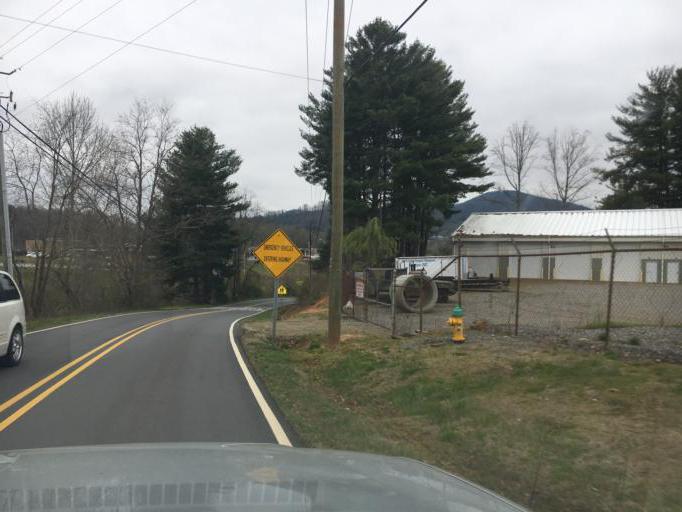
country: US
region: North Carolina
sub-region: Buncombe County
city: Woodfin
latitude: 35.6204
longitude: -82.6202
